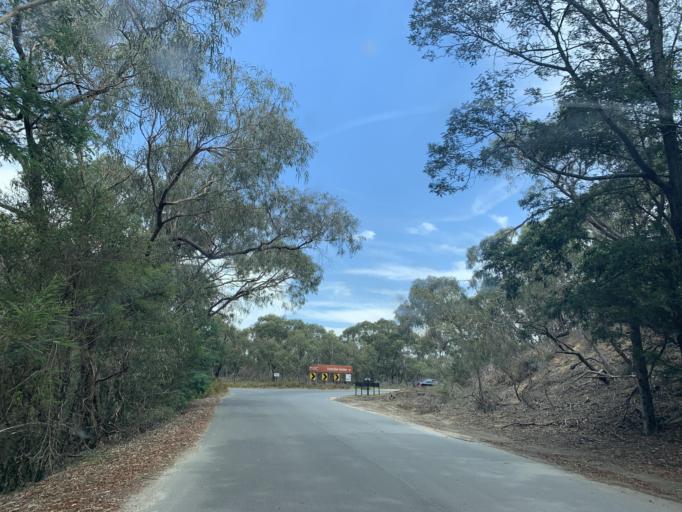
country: AU
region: Victoria
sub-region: Casey
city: Cranbourne
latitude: -38.1273
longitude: 145.2806
